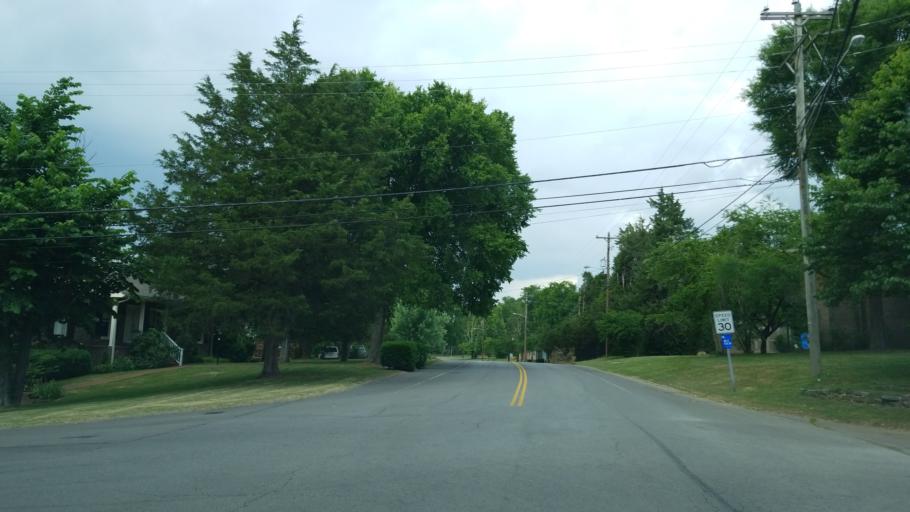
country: US
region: Tennessee
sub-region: Rutherford County
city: La Vergne
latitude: 36.0982
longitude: -86.6081
